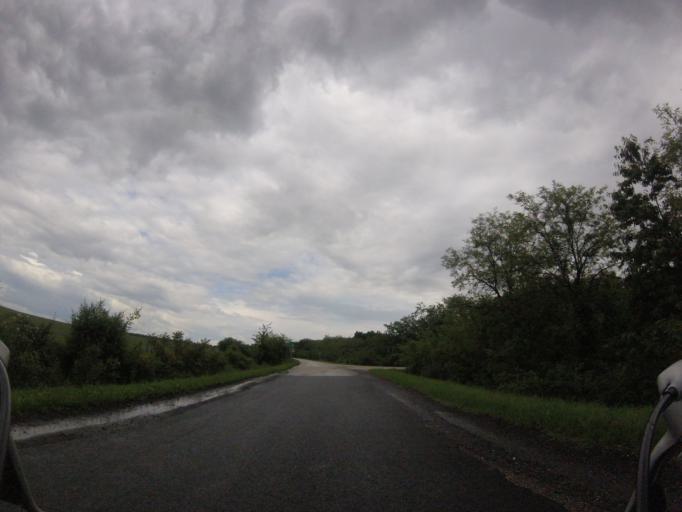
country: HU
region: Baranya
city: Pellerd
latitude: 45.9541
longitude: 18.2122
